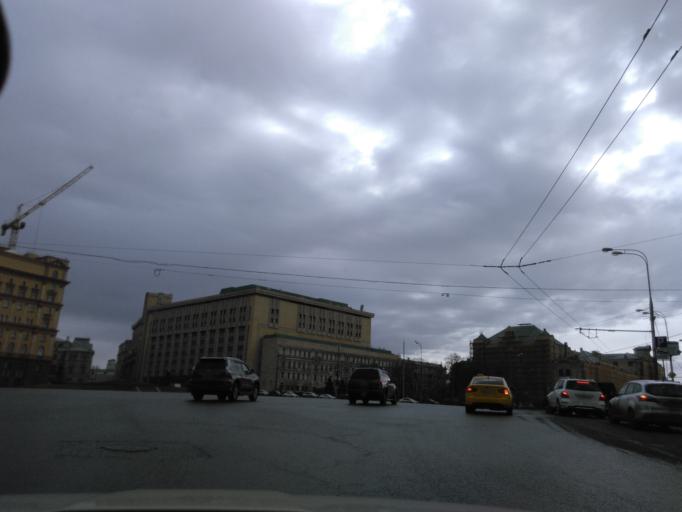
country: RU
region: Moscow
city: Moscow
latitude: 55.7597
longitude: 37.6251
